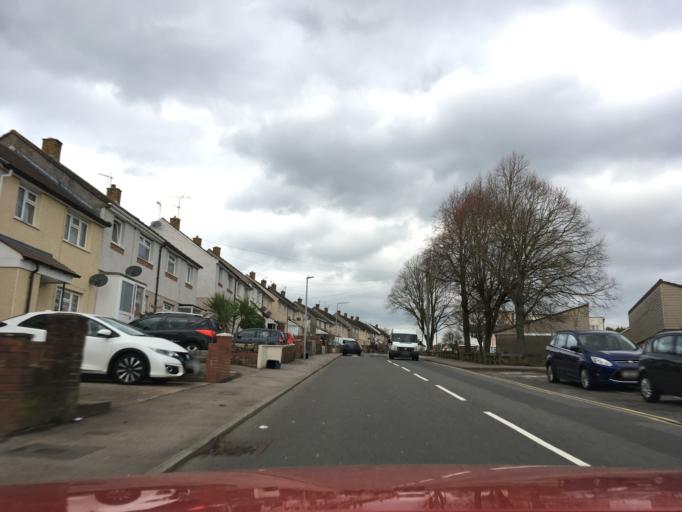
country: GB
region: Wales
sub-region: Monmouthshire
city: Chepstow
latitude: 51.6258
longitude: -2.6707
